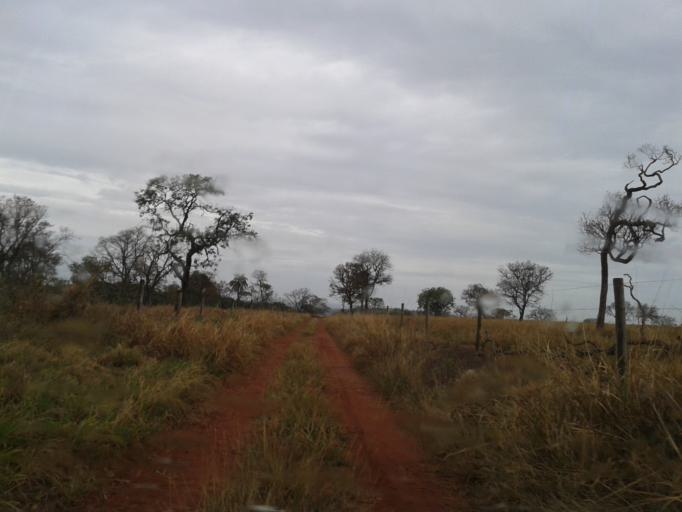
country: BR
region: Minas Gerais
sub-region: Campina Verde
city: Campina Verde
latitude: -19.3485
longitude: -49.5522
